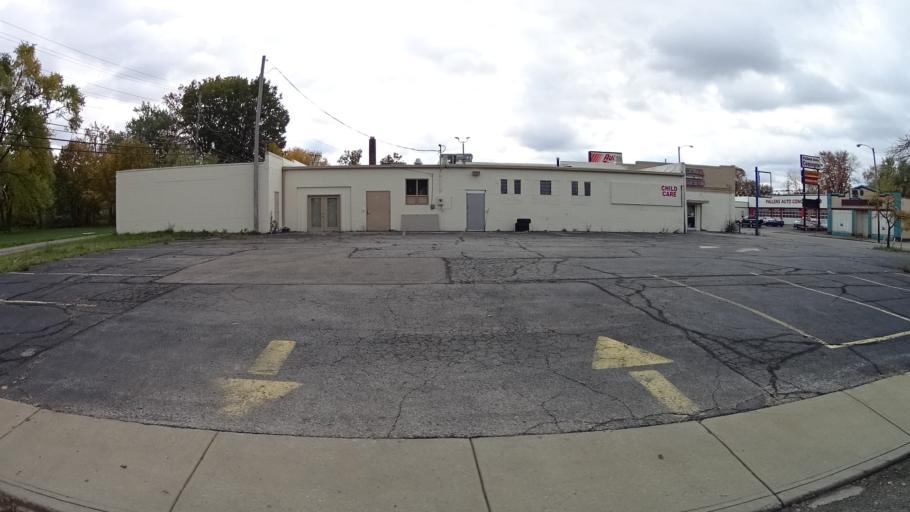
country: US
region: Ohio
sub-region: Lorain County
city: Lorain
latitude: 41.4495
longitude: -82.1654
